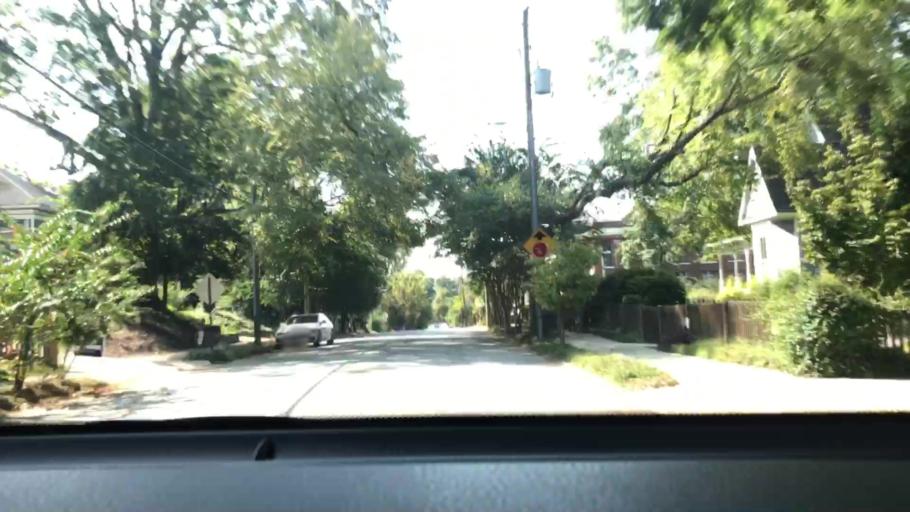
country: US
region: Georgia
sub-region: DeKalb County
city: Druid Hills
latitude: 33.7560
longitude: -84.3232
